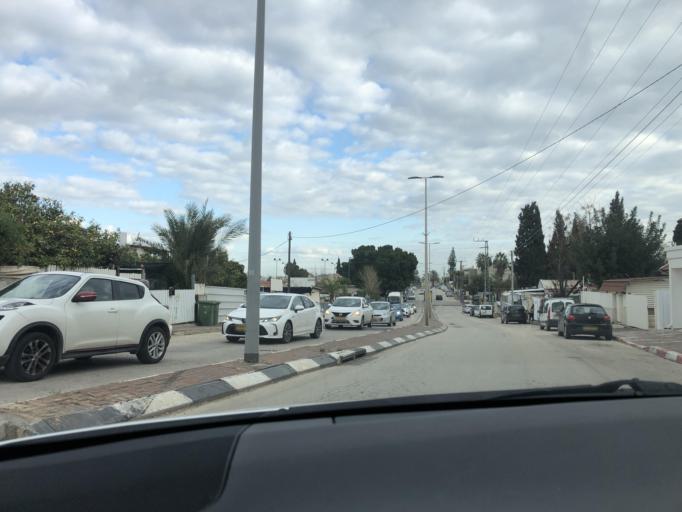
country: IL
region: Central District
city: Rosh Ha'Ayin
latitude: 32.0892
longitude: 34.9538
